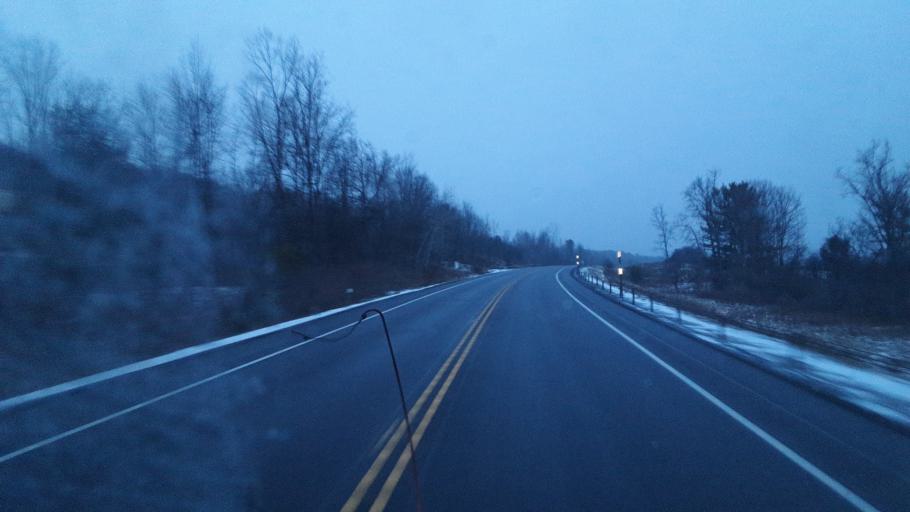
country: US
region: New York
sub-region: Allegany County
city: Belmont
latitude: 42.2667
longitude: -78.0666
